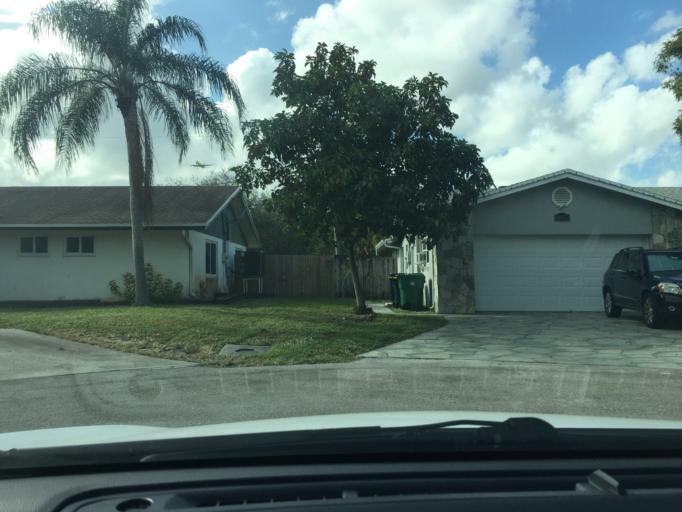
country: US
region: Florida
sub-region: Broward County
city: Dania Beach
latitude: 26.0676
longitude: -80.1733
